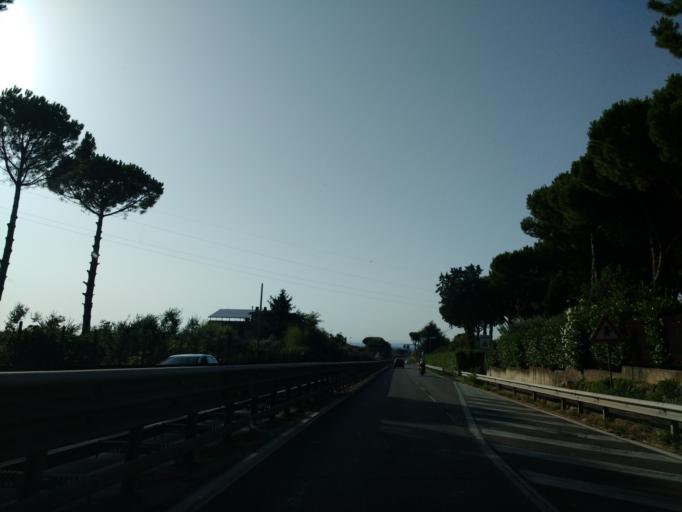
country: IT
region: Latium
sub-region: Citta metropolitana di Roma Capitale
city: Marino
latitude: 41.7604
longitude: 12.6235
